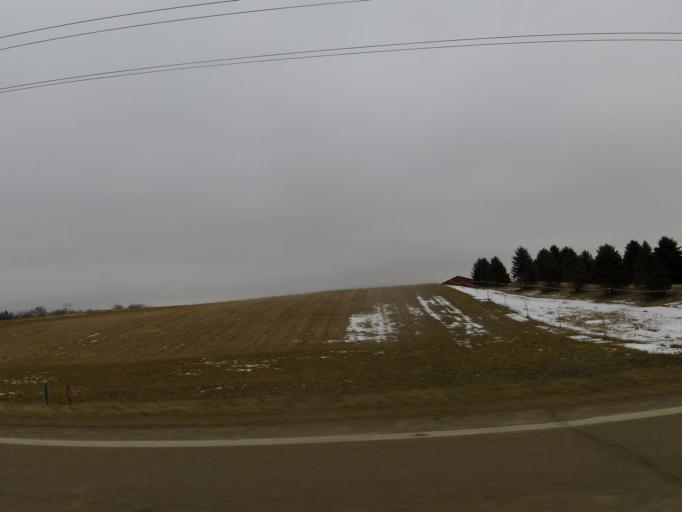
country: US
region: Minnesota
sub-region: Carver County
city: Carver
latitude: 44.7560
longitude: -93.6839
